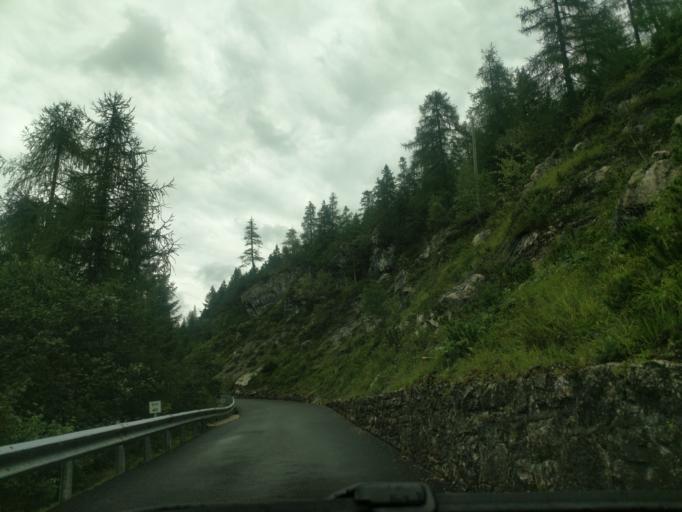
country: IT
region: Veneto
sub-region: Provincia di Belluno
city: La Valle Agordina
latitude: 46.3080
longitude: 12.0831
